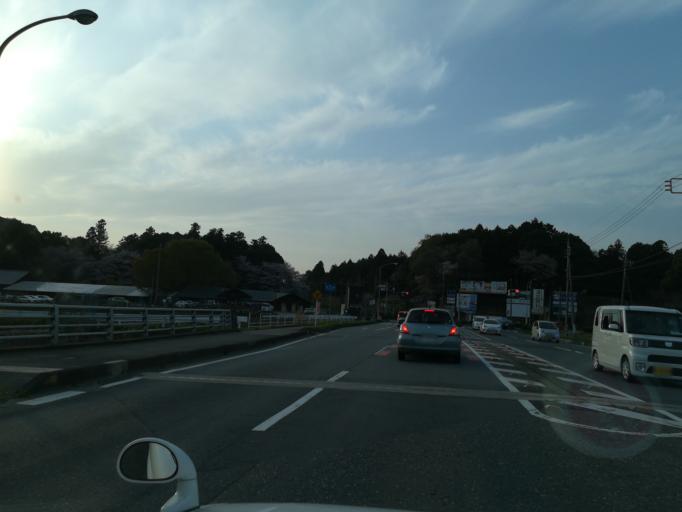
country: JP
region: Ibaraki
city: Naka
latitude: 36.0621
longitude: 140.0817
